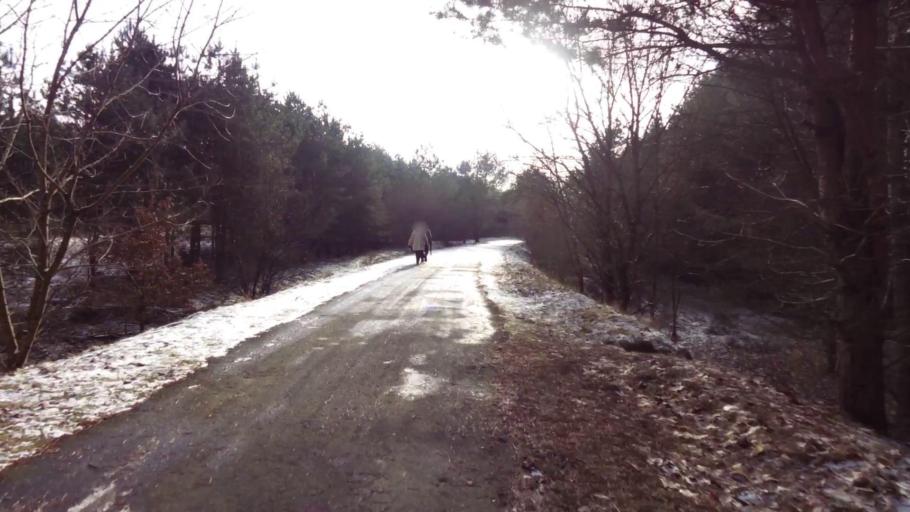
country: PL
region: West Pomeranian Voivodeship
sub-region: Powiat drawski
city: Zlocieniec
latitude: 53.5491
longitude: 16.0194
